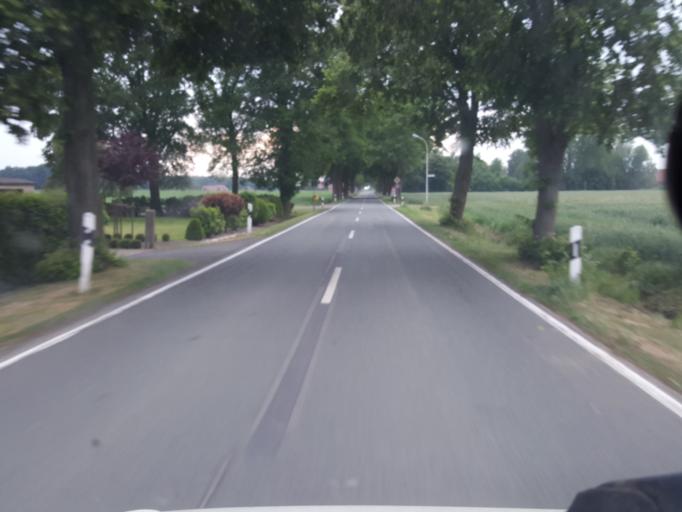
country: DE
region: Lower Saxony
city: Warmsen
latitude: 52.3707
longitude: 8.8745
